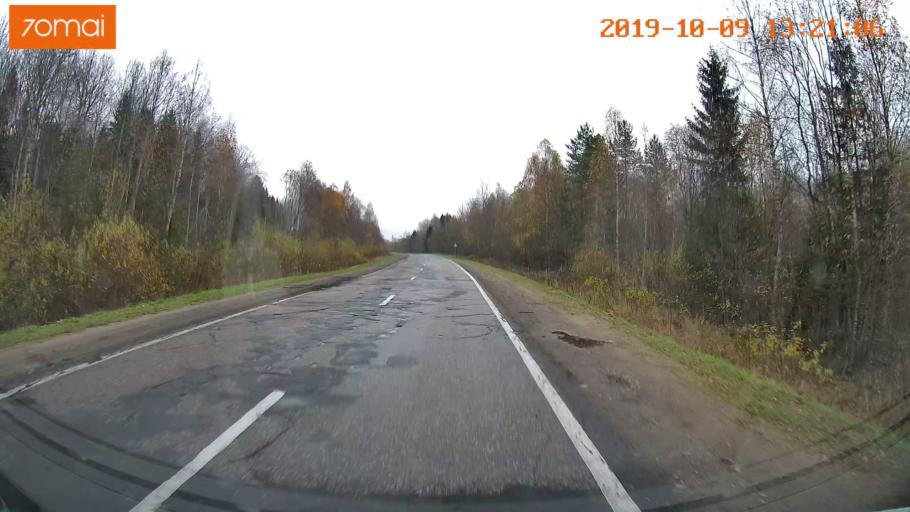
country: RU
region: Jaroslavl
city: Lyubim
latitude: 58.3410
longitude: 40.8405
